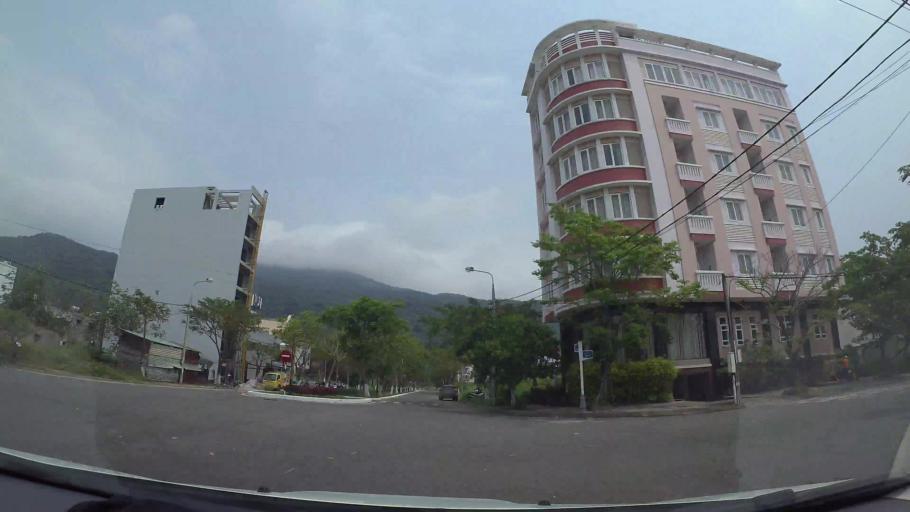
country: VN
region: Da Nang
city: Son Tra
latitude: 16.1051
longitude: 108.2589
